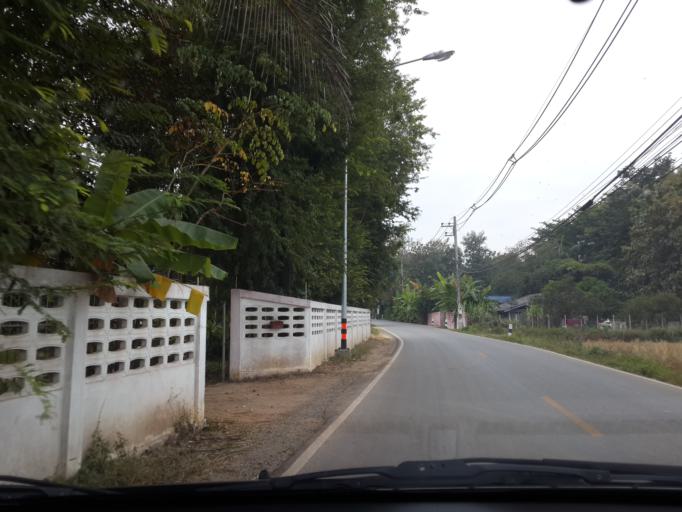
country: TH
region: Chiang Mai
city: San Sai
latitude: 18.8909
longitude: 99.0937
